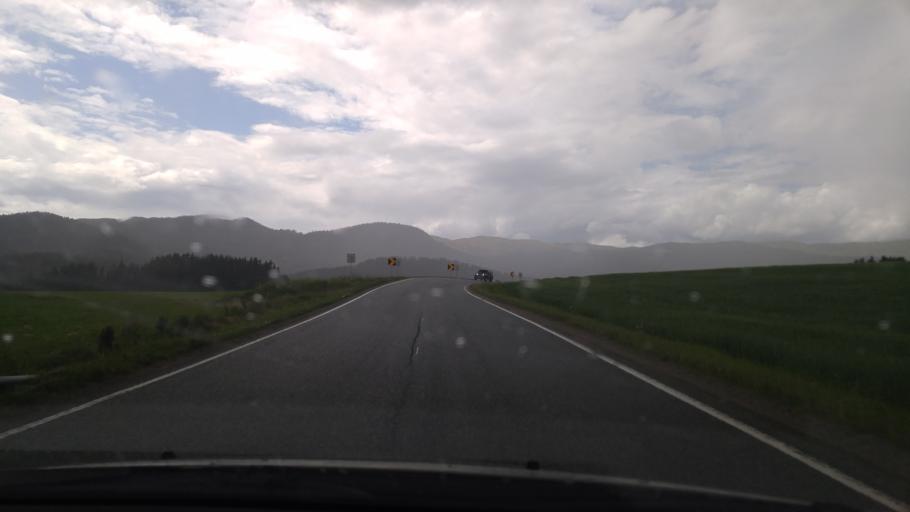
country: NO
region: Nord-Trondelag
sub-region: Namdalseid
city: Namdalseid
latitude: 64.1740
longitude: 11.2394
